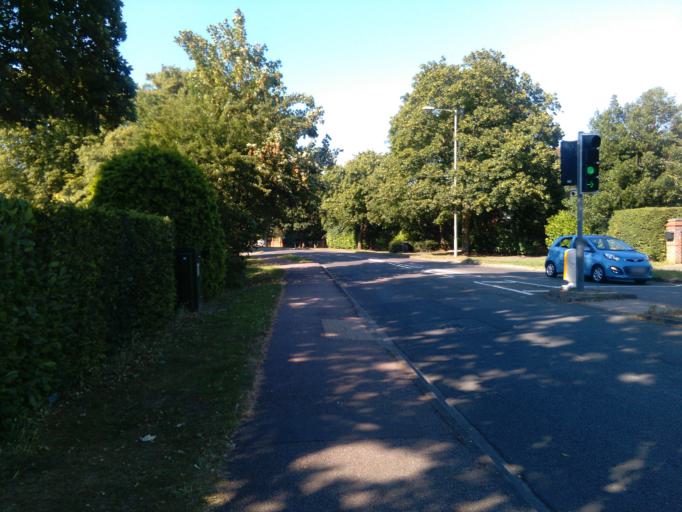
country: GB
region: England
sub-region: Bedford
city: Bedford
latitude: 52.1497
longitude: -0.4541
